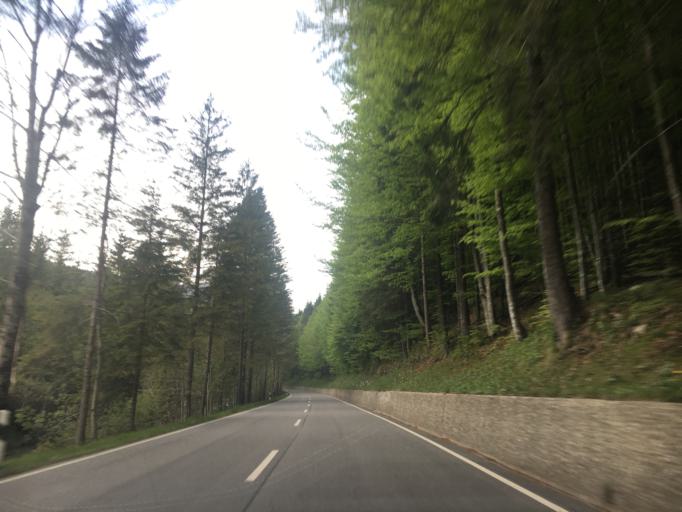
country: DE
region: Bavaria
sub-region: Upper Bavaria
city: Wallgau
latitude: 47.5657
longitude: 11.2965
